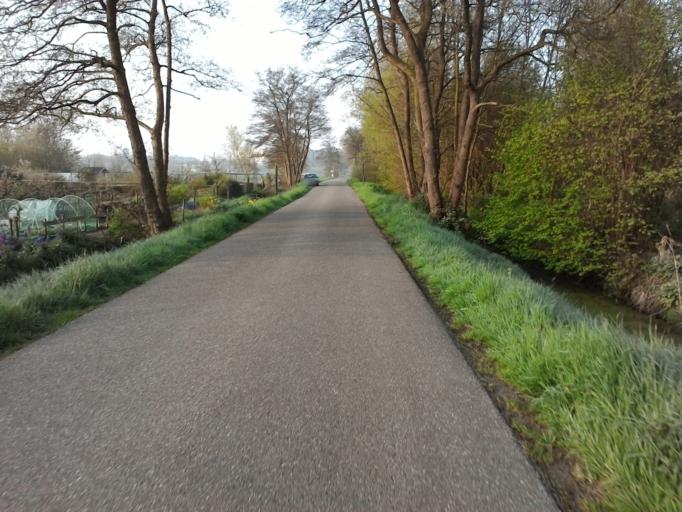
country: NL
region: Utrecht
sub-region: Gemeente Utrecht
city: Utrecht
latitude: 52.1254
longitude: 5.1269
